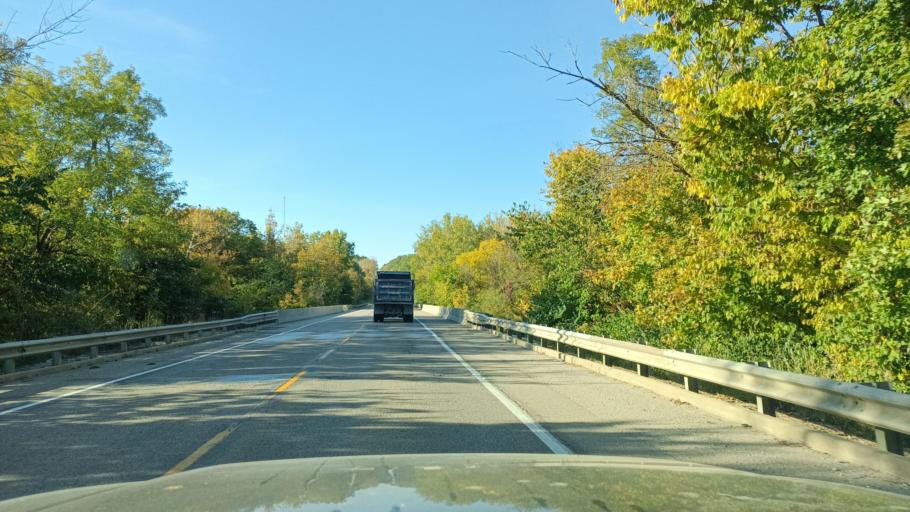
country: US
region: Illinois
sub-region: Clark County
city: Marshall
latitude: 39.4345
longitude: -87.6883
